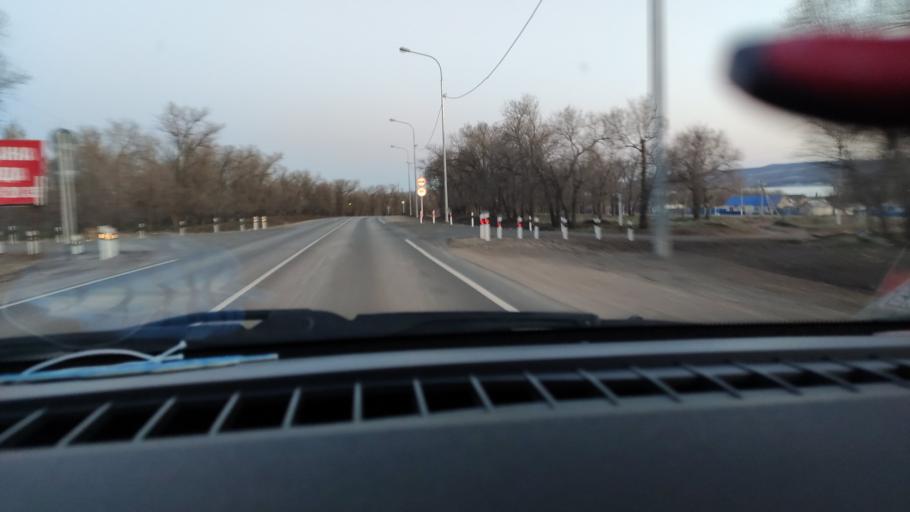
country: RU
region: Saratov
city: Krasnoarmeysk
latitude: 51.0855
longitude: 45.9573
